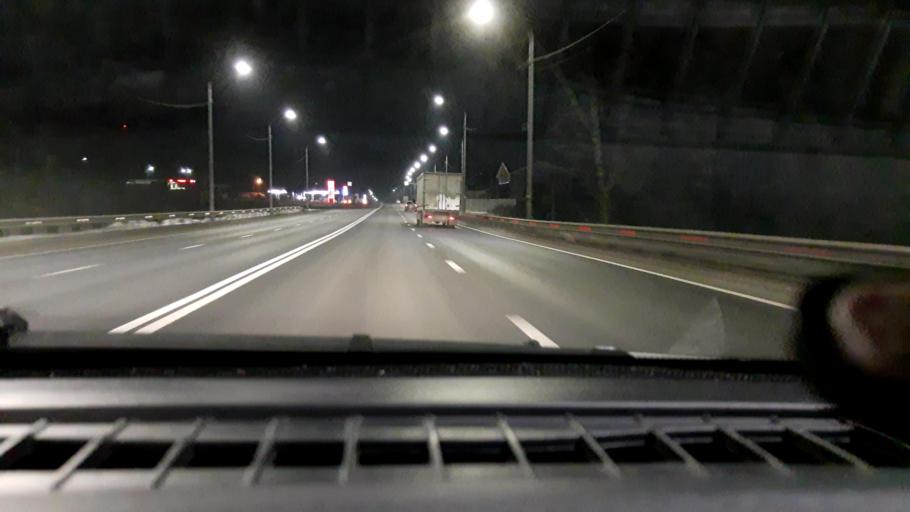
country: RU
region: Nizjnij Novgorod
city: Lyskovo
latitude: 56.0142
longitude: 45.0211
